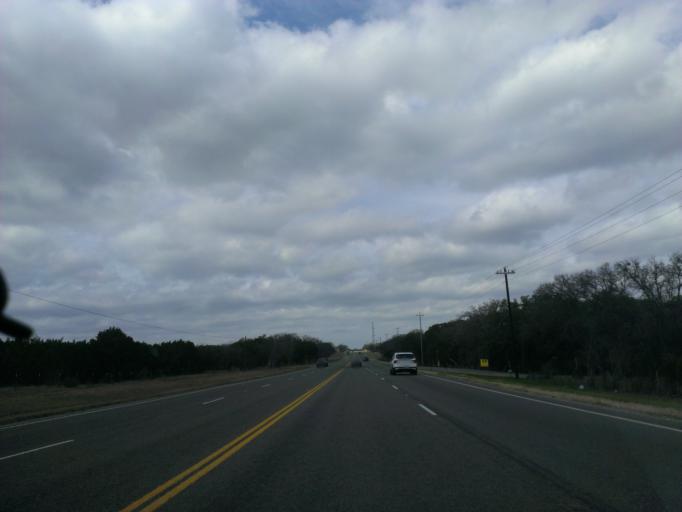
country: US
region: Texas
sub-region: Burnet County
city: Marble Falls
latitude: 30.4740
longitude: -98.1835
